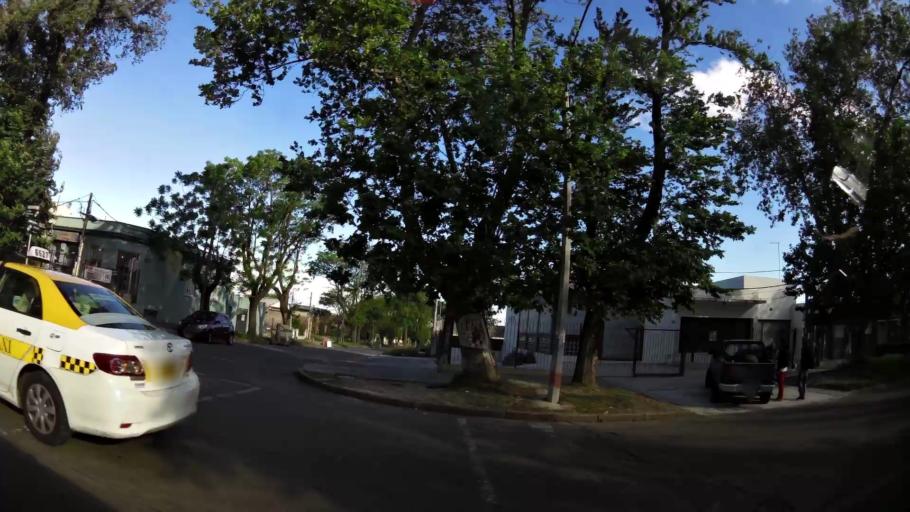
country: UY
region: Montevideo
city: Montevideo
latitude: -34.8619
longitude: -56.2309
